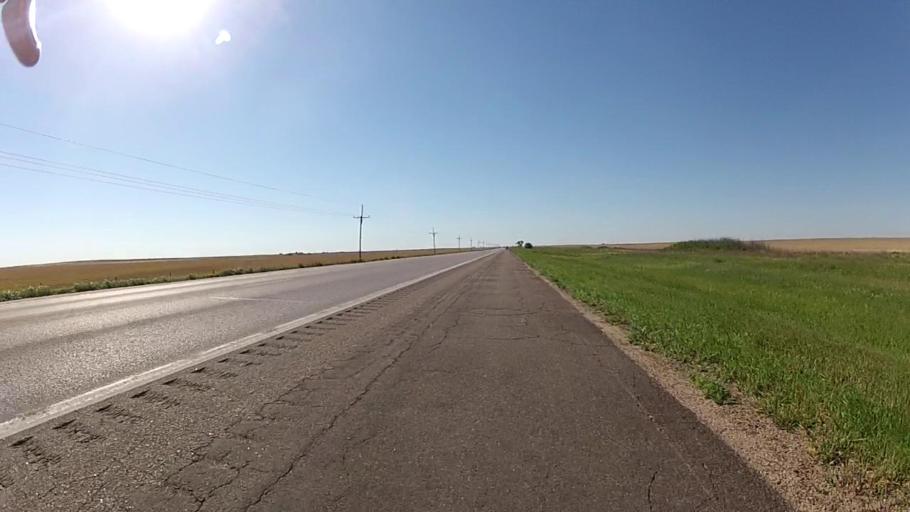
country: US
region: Kansas
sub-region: Ford County
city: Dodge City
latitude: 37.5992
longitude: -99.6996
